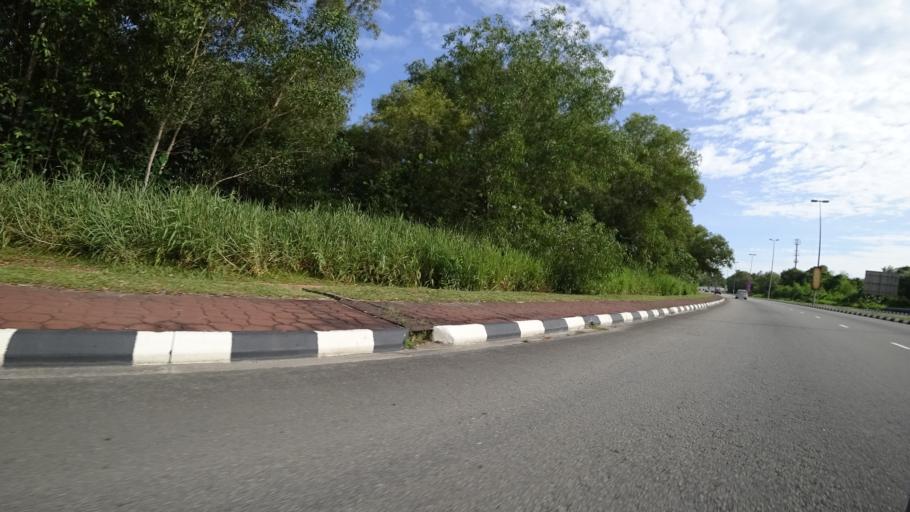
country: BN
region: Brunei and Muara
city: Bandar Seri Begawan
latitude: 4.8996
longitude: 114.9170
